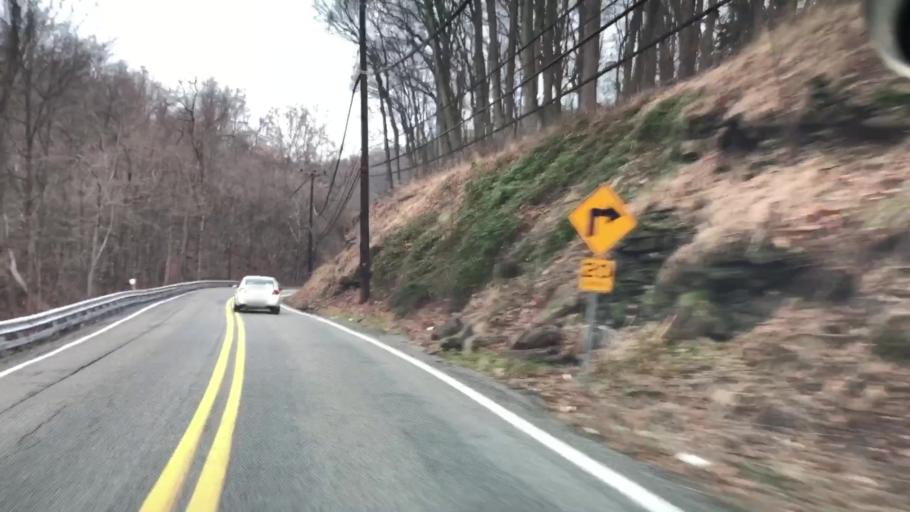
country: US
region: Pennsylvania
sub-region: Allegheny County
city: Penn Hills
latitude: 40.4712
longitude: -79.8307
